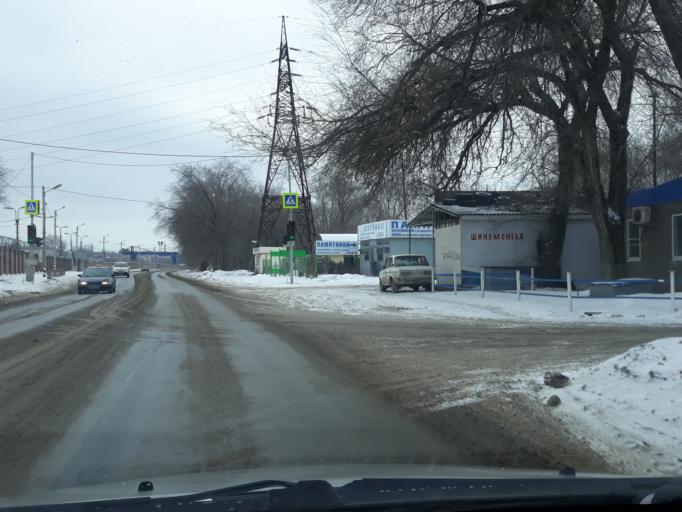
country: RU
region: Rostov
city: Taganrog
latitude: 47.2564
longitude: 38.9027
